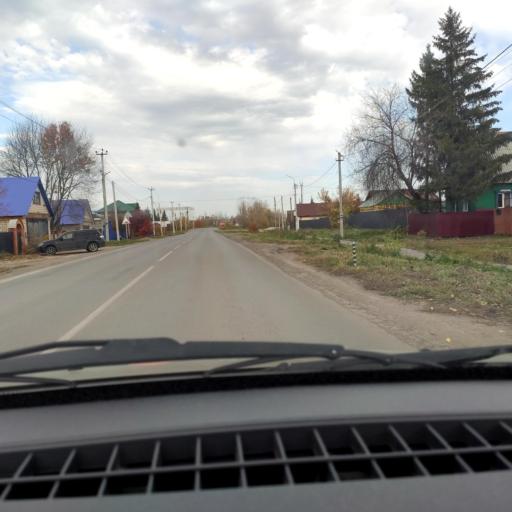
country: RU
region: Bashkortostan
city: Ufa
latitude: 54.6198
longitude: 55.9064
